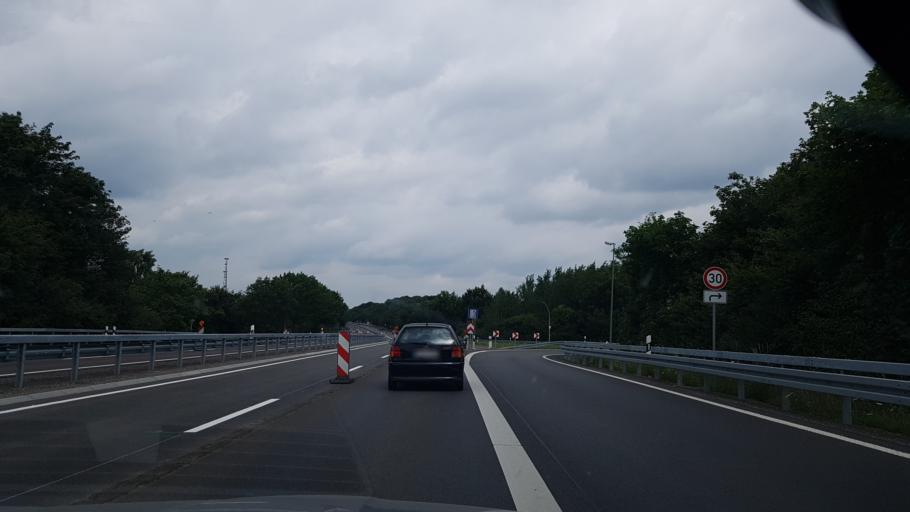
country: DE
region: Schleswig-Holstein
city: Neumunster
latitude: 54.0997
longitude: 9.9740
